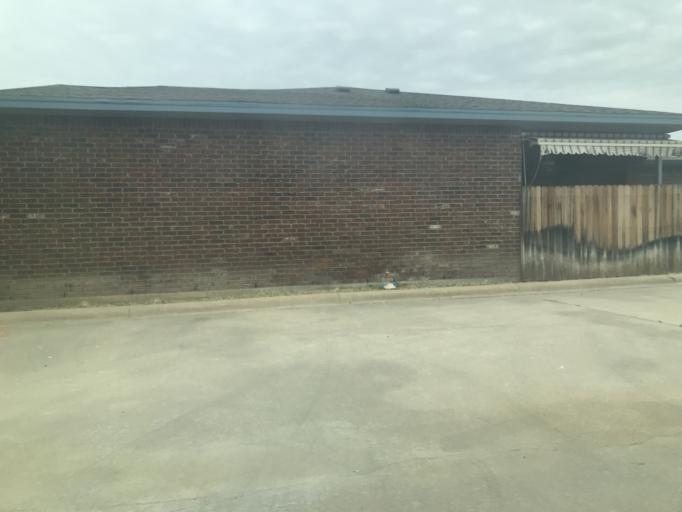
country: US
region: Texas
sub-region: Tom Green County
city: San Angelo
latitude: 31.4203
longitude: -100.4777
